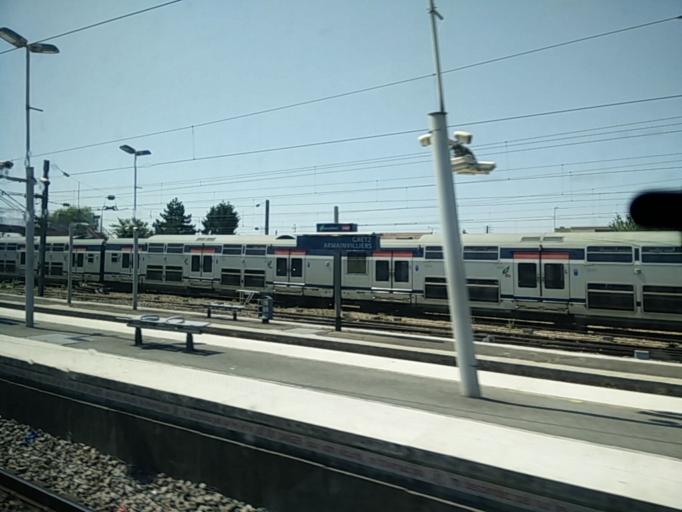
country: FR
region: Ile-de-France
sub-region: Departement de Seine-et-Marne
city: Gretz-Armainvilliers
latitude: 48.7462
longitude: 2.7276
